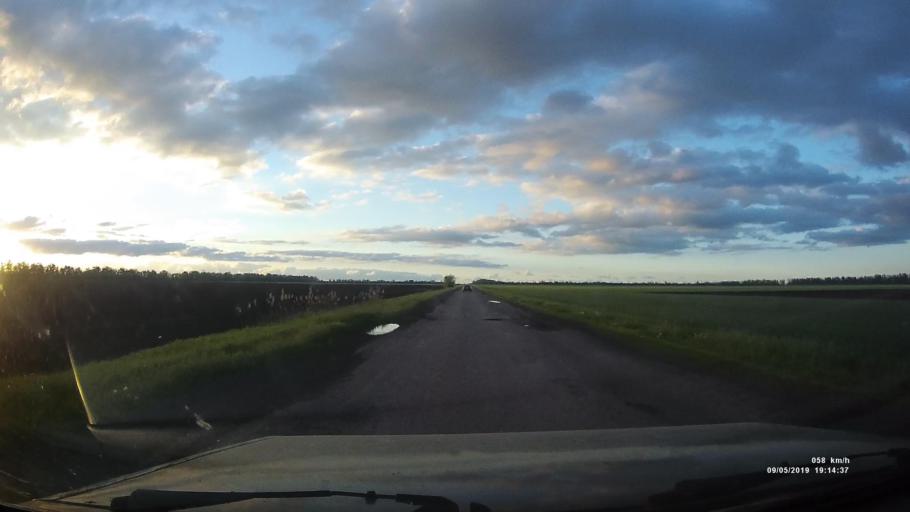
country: RU
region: Krasnodarskiy
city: Kanelovskaya
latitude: 46.7600
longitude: 39.2139
